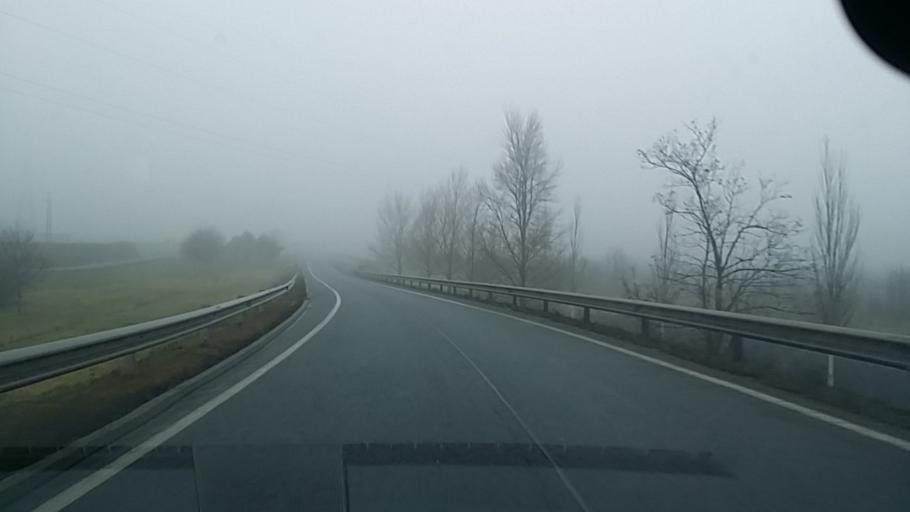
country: HU
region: Gyor-Moson-Sopron
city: Mosonmagyarovar
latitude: 47.8532
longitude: 17.2490
